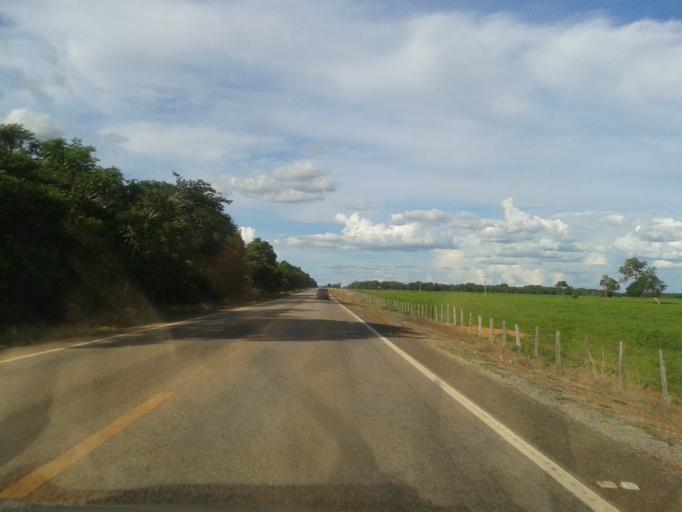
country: BR
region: Goias
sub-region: Mozarlandia
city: Mozarlandia
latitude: -14.3264
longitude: -50.4123
